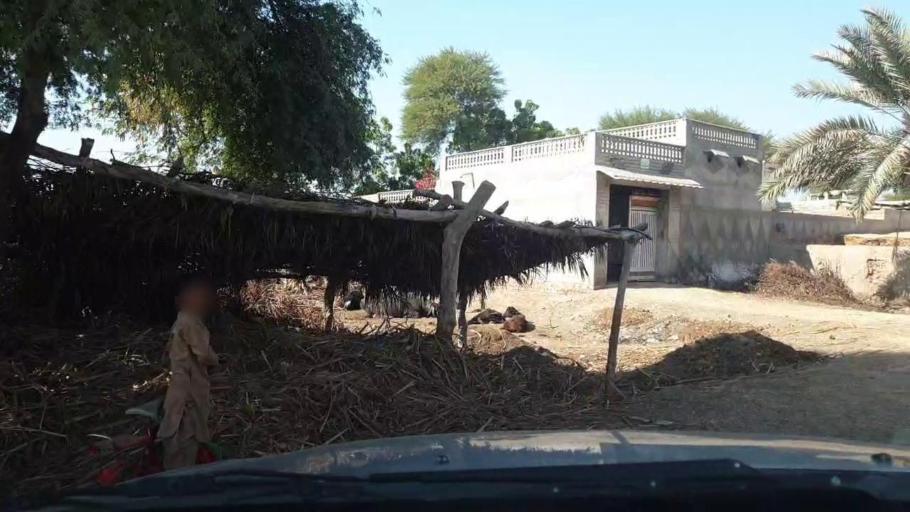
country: PK
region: Sindh
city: Mirpur Mathelo
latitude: 28.0311
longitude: 69.5497
